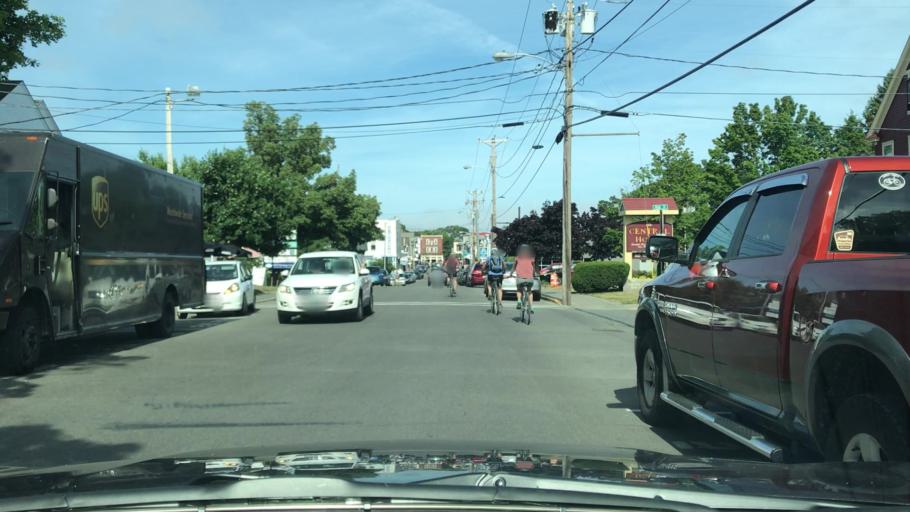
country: US
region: Maine
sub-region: Hancock County
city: Bar Harbor
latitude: 44.3892
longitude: -68.2085
